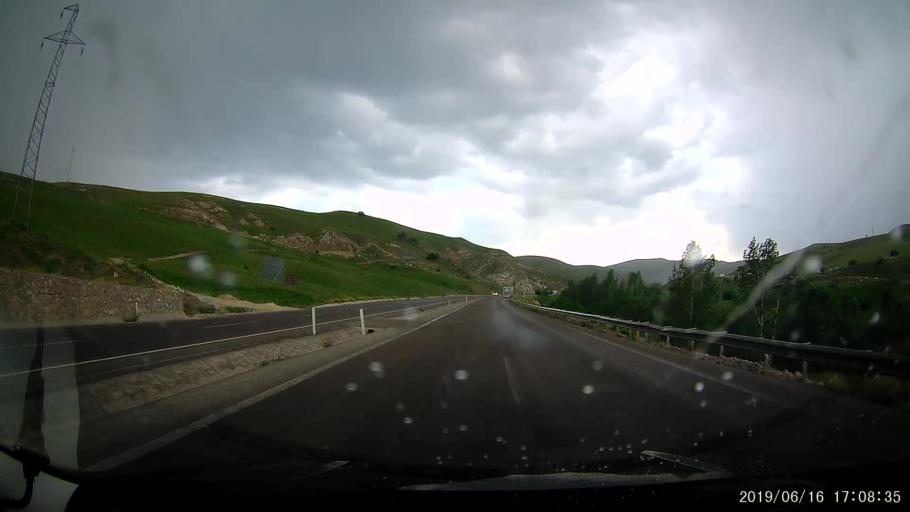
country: TR
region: Erzurum
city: Askale
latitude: 39.9068
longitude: 40.6597
